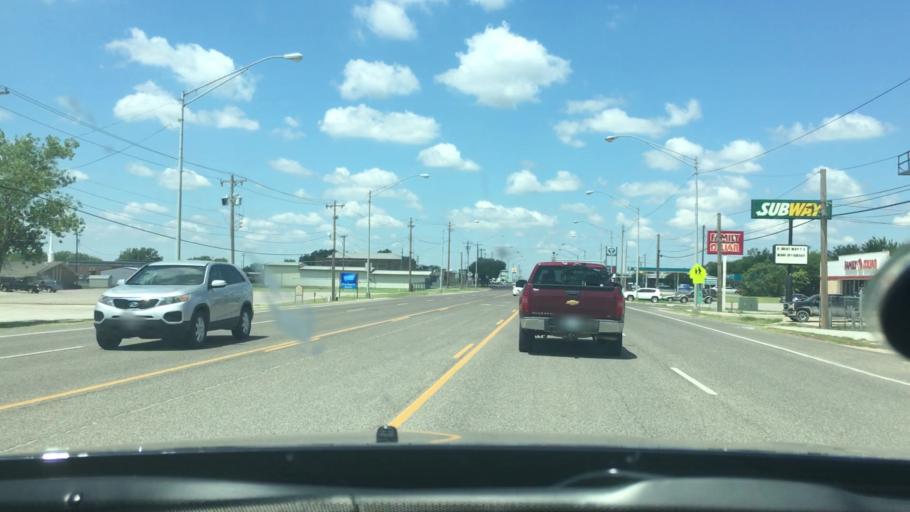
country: US
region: Oklahoma
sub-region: Carter County
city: Lone Grove
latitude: 34.1730
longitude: -97.2588
